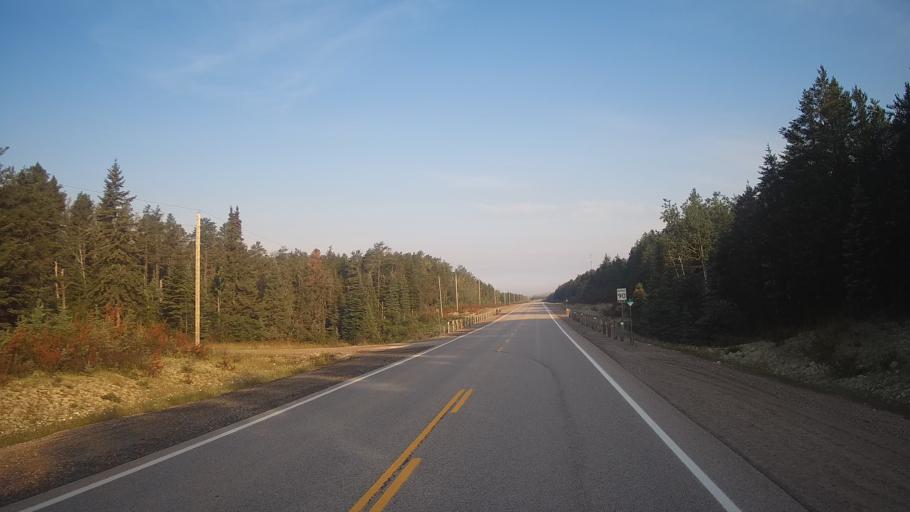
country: CA
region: Ontario
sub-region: Rainy River District
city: Atikokan
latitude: 49.3263
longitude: -91.4165
